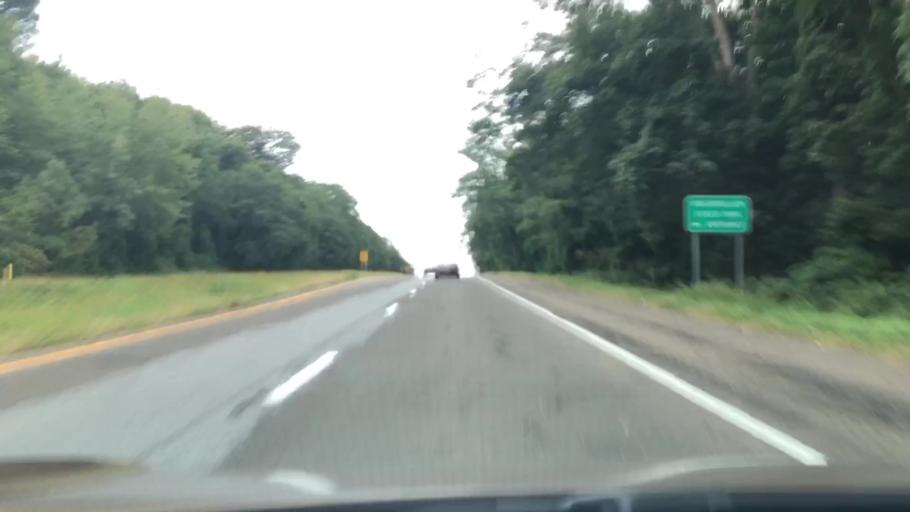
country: US
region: New York
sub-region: Westchester County
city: Briarcliff Manor
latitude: 41.1144
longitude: -73.8318
